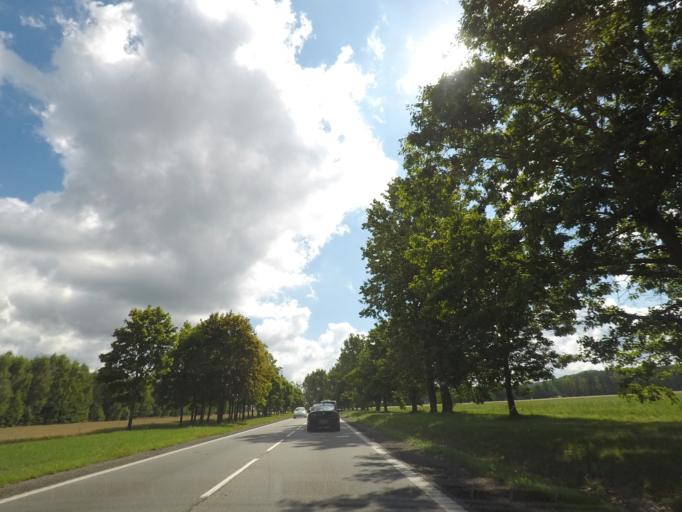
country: PL
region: Pomeranian Voivodeship
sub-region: Powiat wejherowski
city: Leczyce
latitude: 54.5700
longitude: 17.9579
